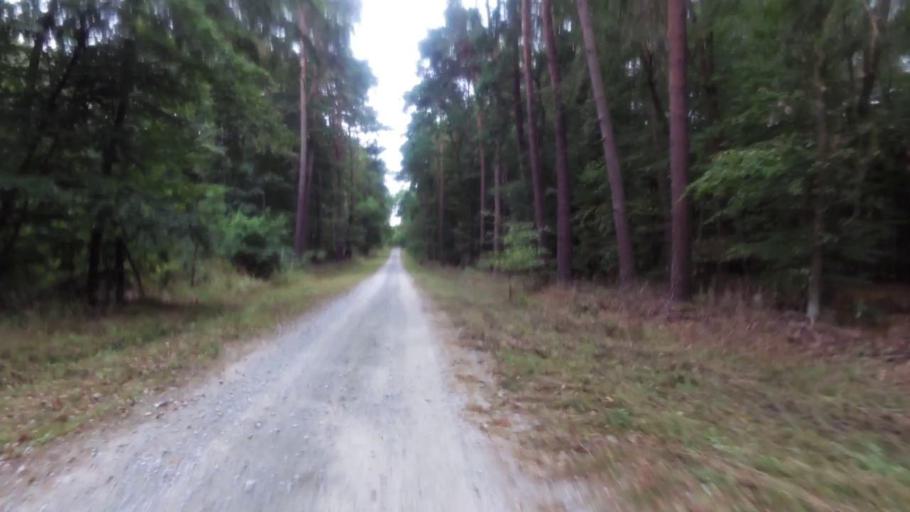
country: PL
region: Lubusz
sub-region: Powiat gorzowski
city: Kostrzyn nad Odra
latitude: 52.6264
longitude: 14.6478
